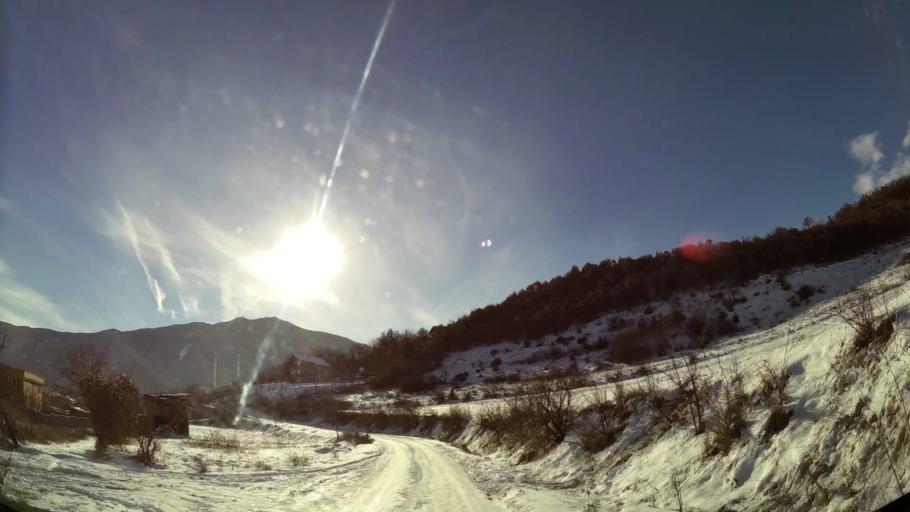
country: MK
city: Ljubin
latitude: 41.9818
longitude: 21.3003
